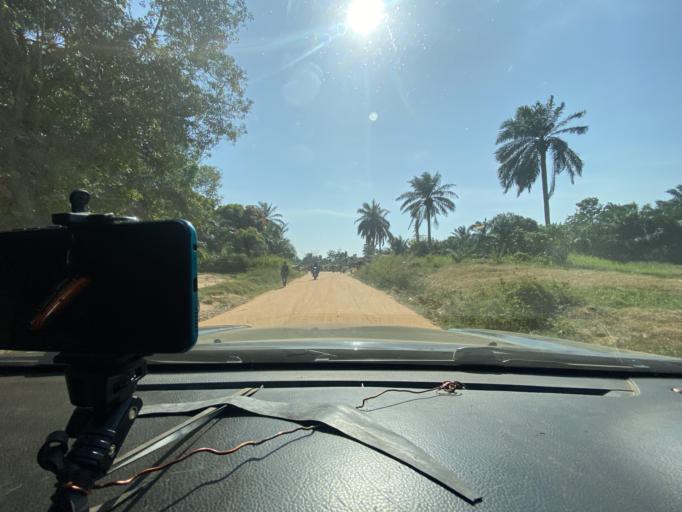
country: CD
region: Kasai-Oriental
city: Kabinda
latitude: -6.1307
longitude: 24.5257
